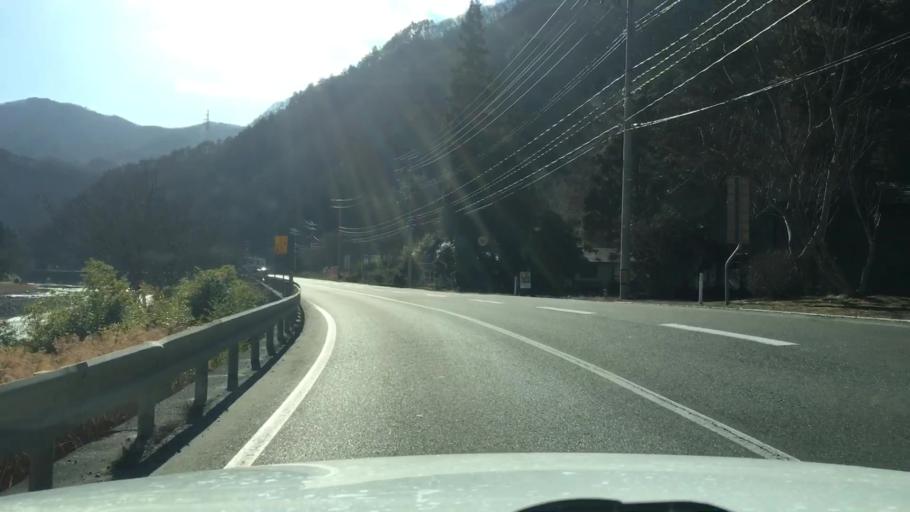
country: JP
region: Iwate
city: Miyako
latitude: 39.6179
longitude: 141.7906
